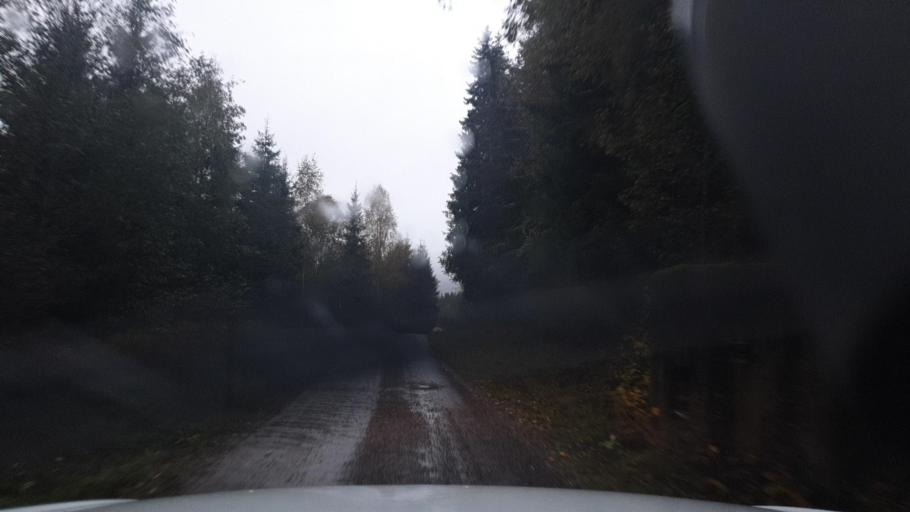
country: SE
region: Vaermland
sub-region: Eda Kommun
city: Amotfors
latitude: 59.7960
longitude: 12.4255
